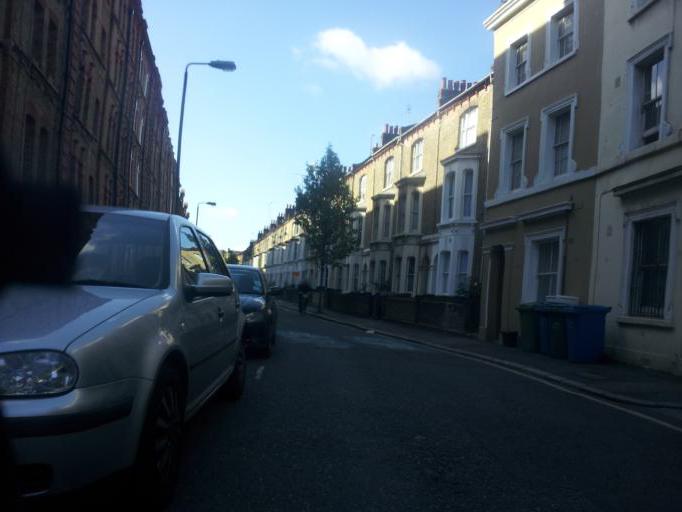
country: GB
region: England
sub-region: Greater London
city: Kennington
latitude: 51.4952
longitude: -0.1032
